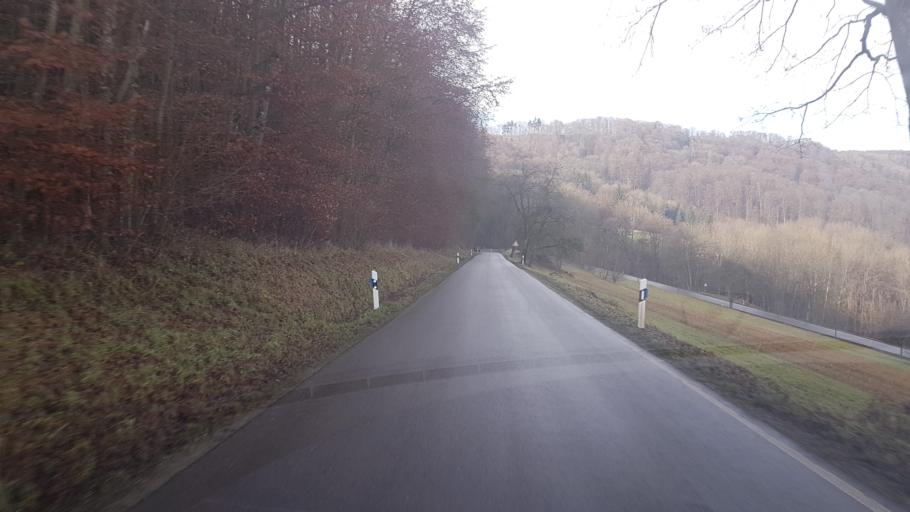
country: DE
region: Baden-Wuerttemberg
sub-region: Regierungsbezirk Stuttgart
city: Braunsbach
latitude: 49.2015
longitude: 9.7770
